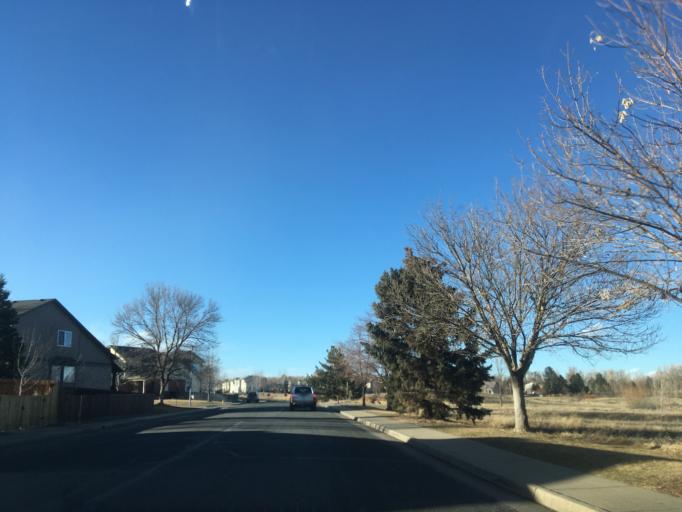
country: US
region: Colorado
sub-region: Adams County
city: Northglenn
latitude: 39.9252
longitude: -104.9548
